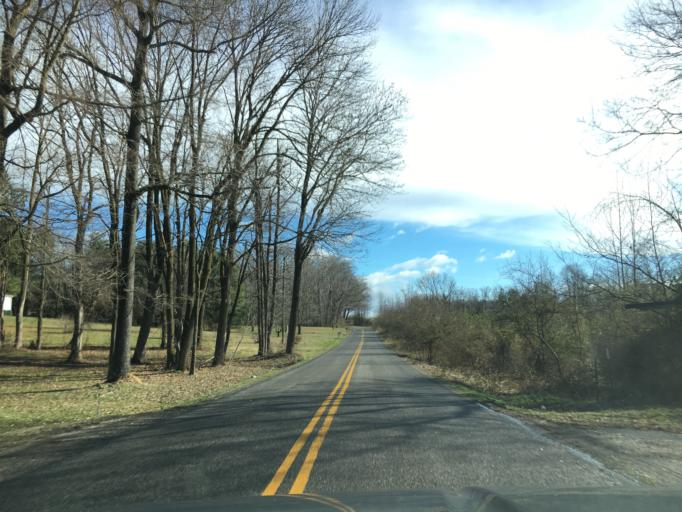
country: US
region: Virginia
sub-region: Amelia County
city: Amelia Court House
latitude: 37.4459
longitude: -77.9987
